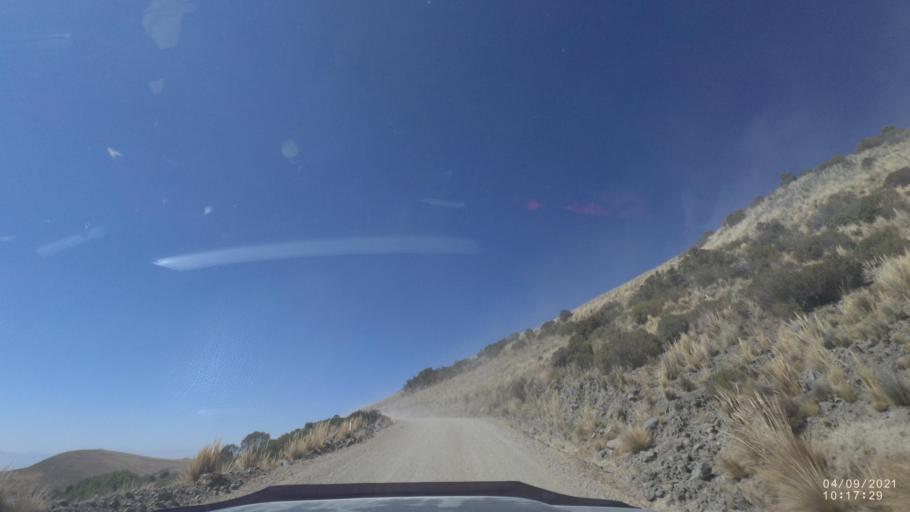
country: BO
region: Cochabamba
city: Sipe Sipe
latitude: -17.3205
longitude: -66.4220
